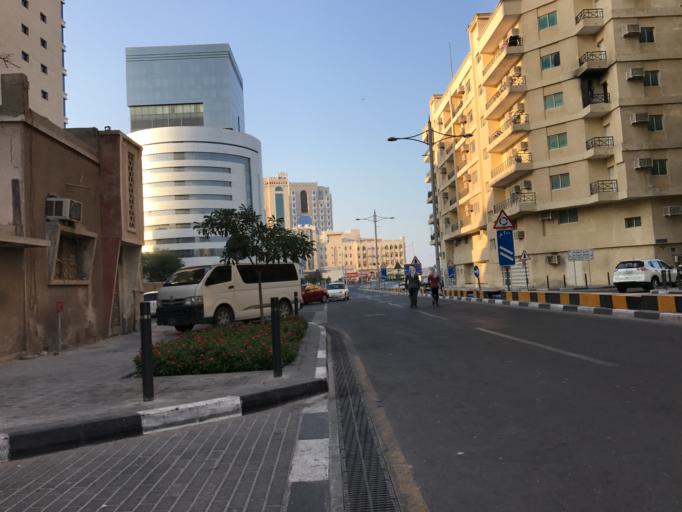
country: QA
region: Baladiyat ad Dawhah
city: Doha
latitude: 25.2850
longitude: 51.5475
